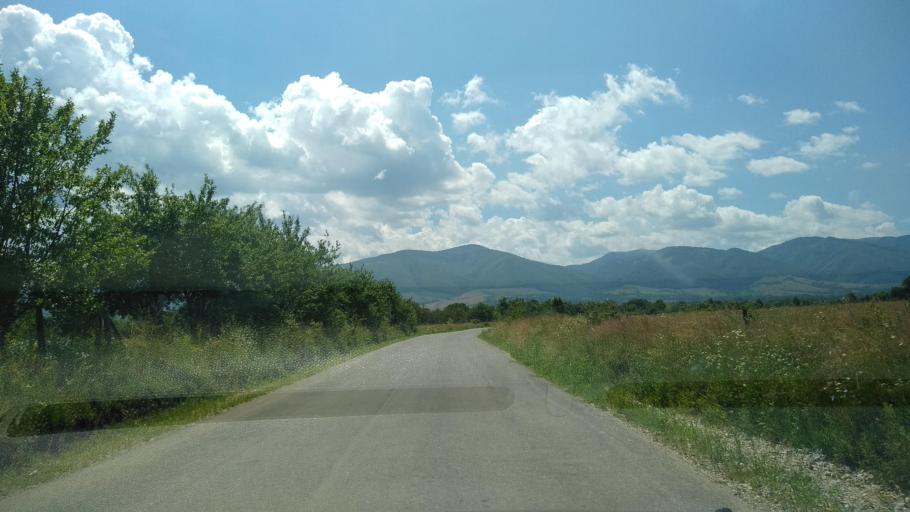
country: RO
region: Hunedoara
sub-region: Comuna Sarmizegetusa
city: Sarmizegetusa
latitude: 45.5389
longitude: 22.8180
